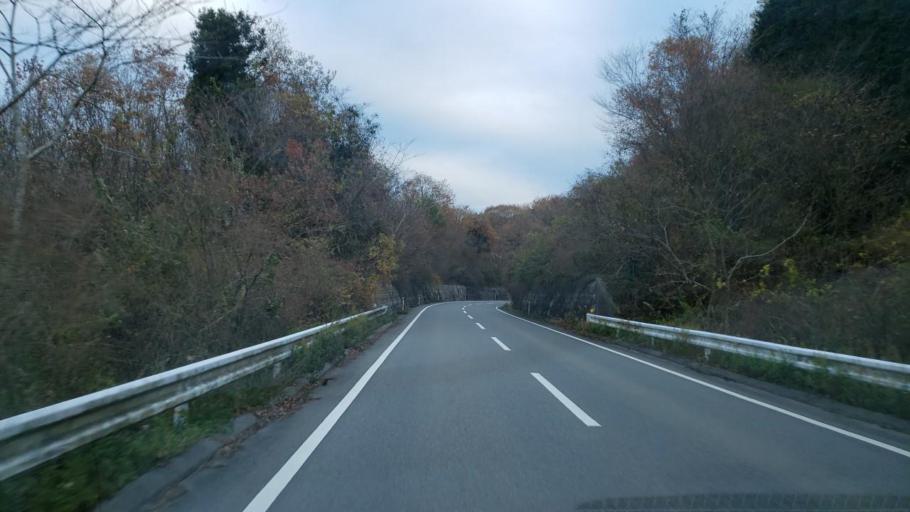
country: JP
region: Tokushima
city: Wakimachi
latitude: 34.1829
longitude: 134.1783
